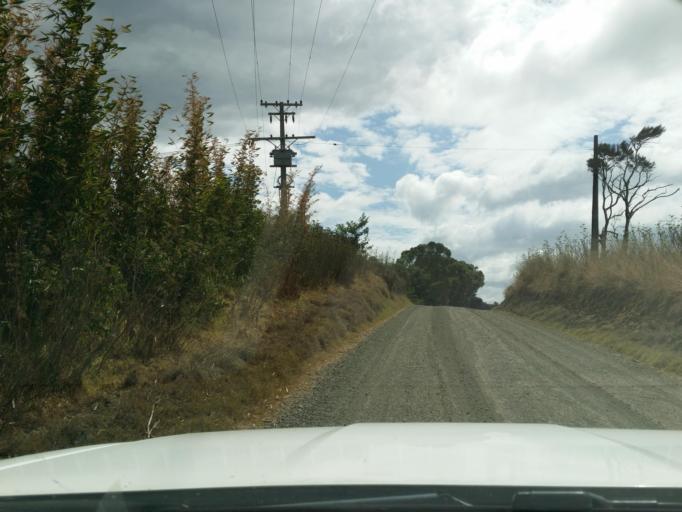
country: NZ
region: Auckland
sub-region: Auckland
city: Wellsford
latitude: -36.3374
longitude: 174.1592
